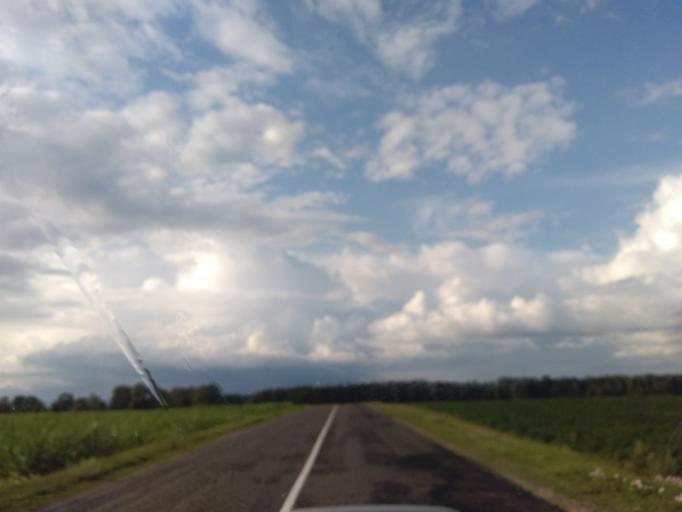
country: BY
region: Minsk
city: Kapyl'
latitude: 53.2821
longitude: 27.0806
